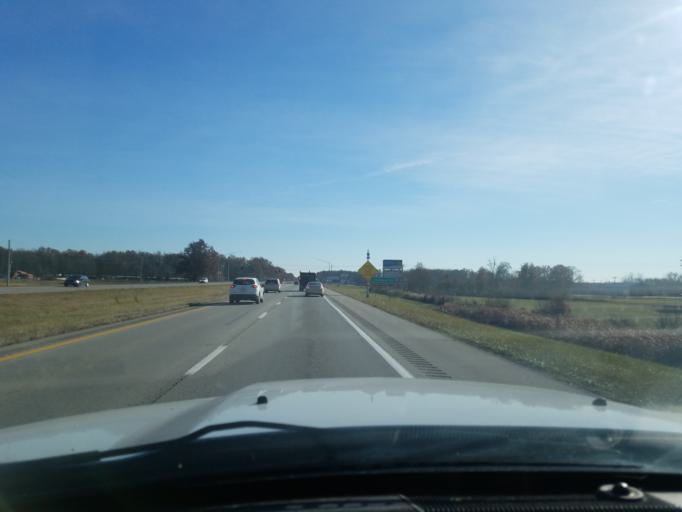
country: US
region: Ohio
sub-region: Clermont County
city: Williamsburg
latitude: 39.0567
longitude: -83.9858
